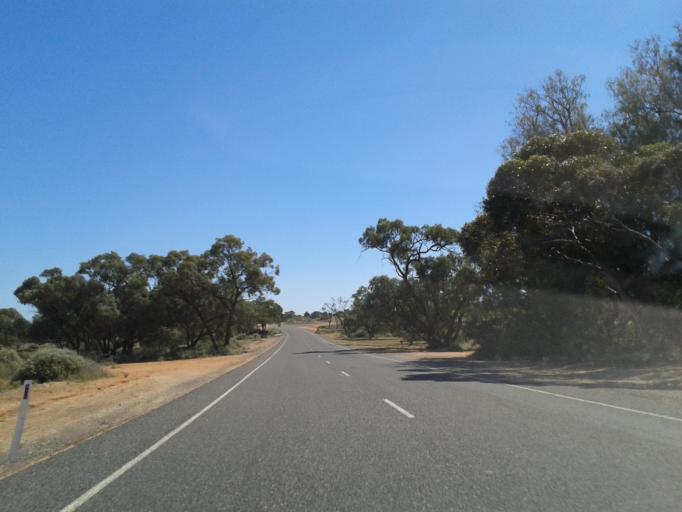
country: AU
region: New South Wales
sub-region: Wentworth
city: Dareton
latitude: -34.1458
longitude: 141.9970
